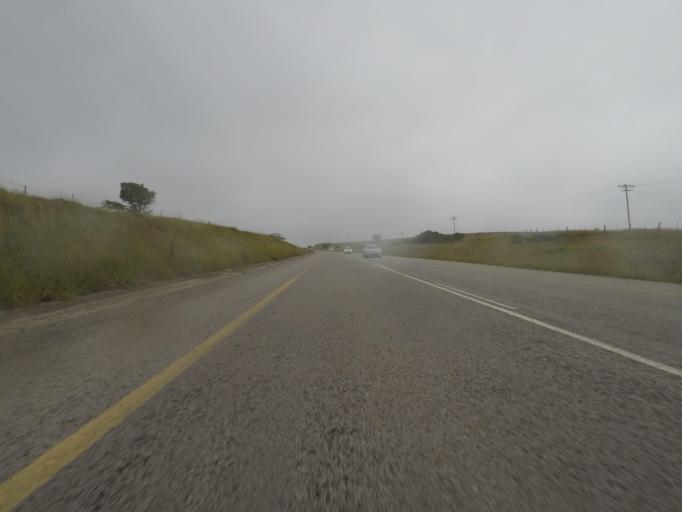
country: ZA
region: Eastern Cape
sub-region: Cacadu District Municipality
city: Grahamstown
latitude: -33.6364
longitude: 26.3203
